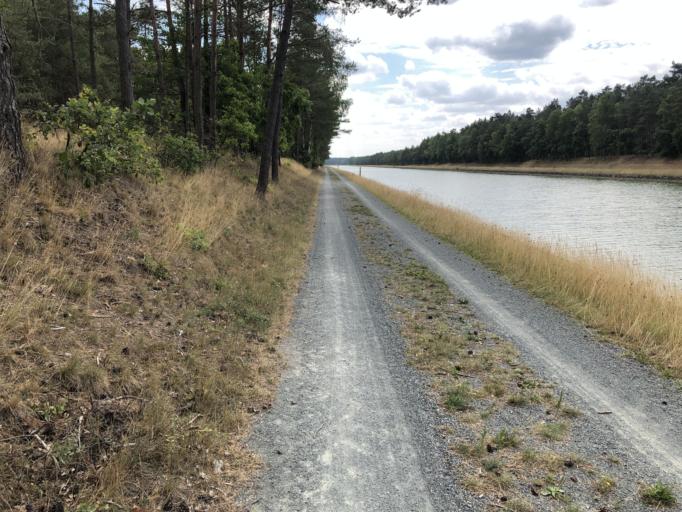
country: DE
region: Lower Saxony
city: Wendisch Evern
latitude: 53.2031
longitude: 10.4981
